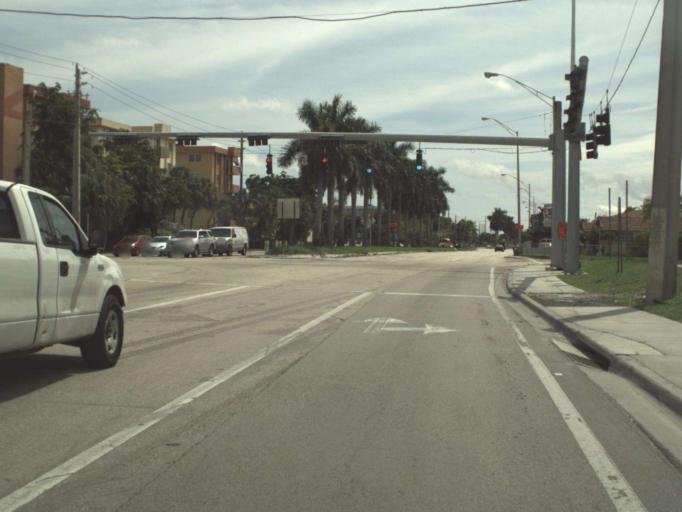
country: US
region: Florida
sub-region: Miami-Dade County
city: Flagami
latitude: 25.7770
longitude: -80.3126
